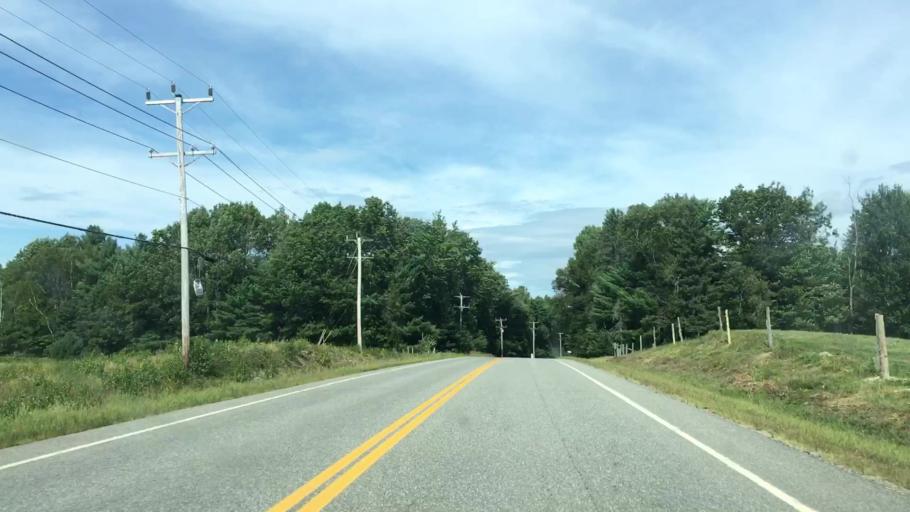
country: US
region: Maine
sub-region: Penobscot County
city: Lincoln
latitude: 45.3998
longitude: -68.5092
